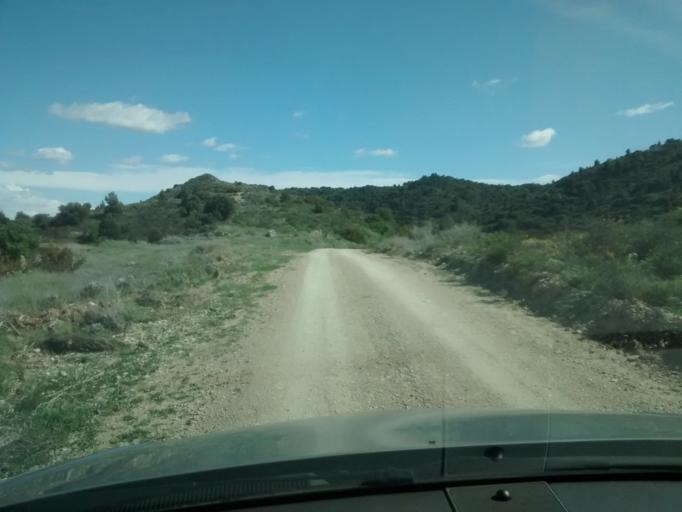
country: ES
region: Aragon
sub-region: Provincia de Huesca
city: Alcubierre
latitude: 41.8173
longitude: -0.5092
